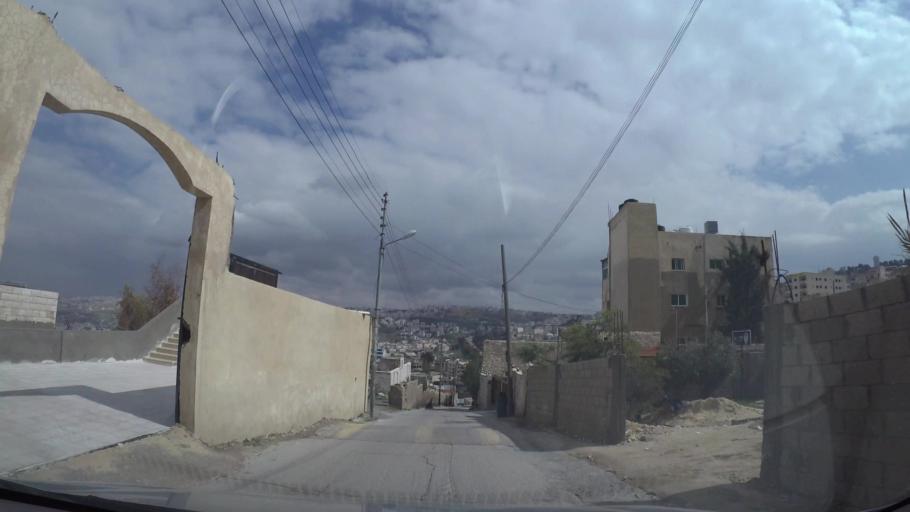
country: JO
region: Amman
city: Al Jubayhah
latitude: 32.0352
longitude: 35.8249
